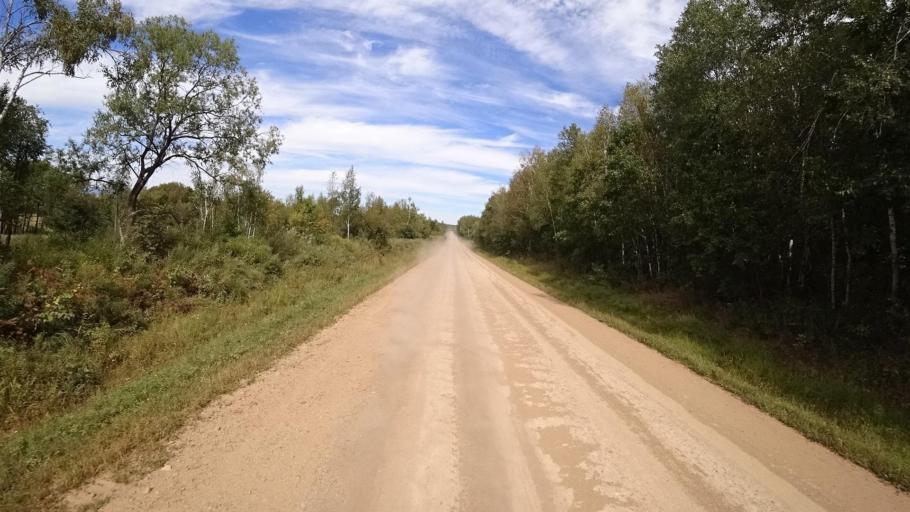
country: RU
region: Primorskiy
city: Yakovlevka
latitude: 44.5775
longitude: 133.5959
